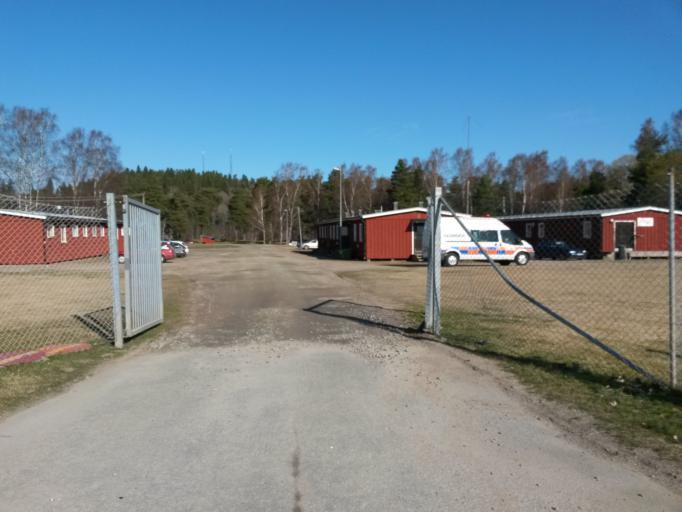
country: SE
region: Vaestra Goetaland
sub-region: Vargarda Kommun
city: Vargarda
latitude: 58.0296
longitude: 12.8354
